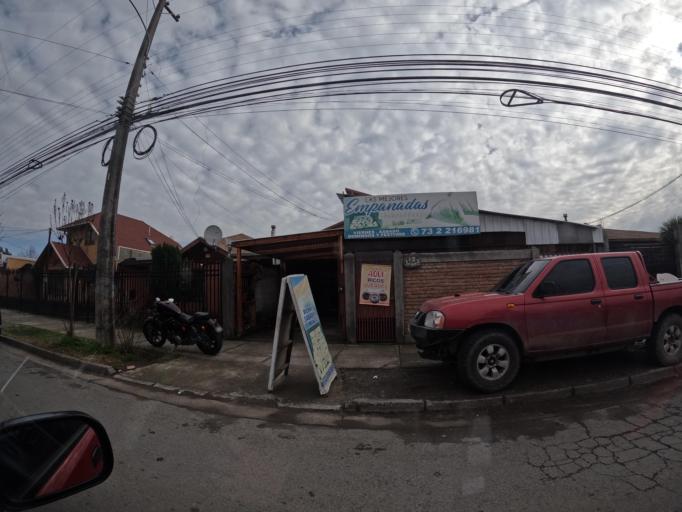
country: CL
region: Maule
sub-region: Provincia de Linares
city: Linares
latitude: -35.8371
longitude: -71.6024
